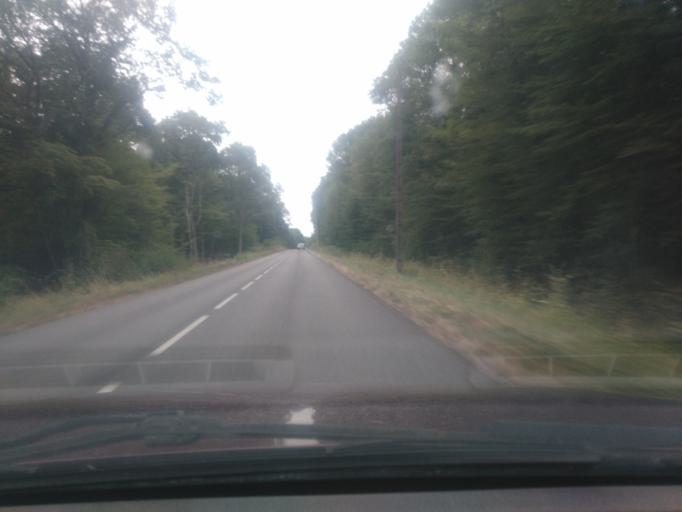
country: FR
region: Bourgogne
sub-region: Departement de la Nievre
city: Dornes
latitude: 46.7720
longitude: 3.3298
